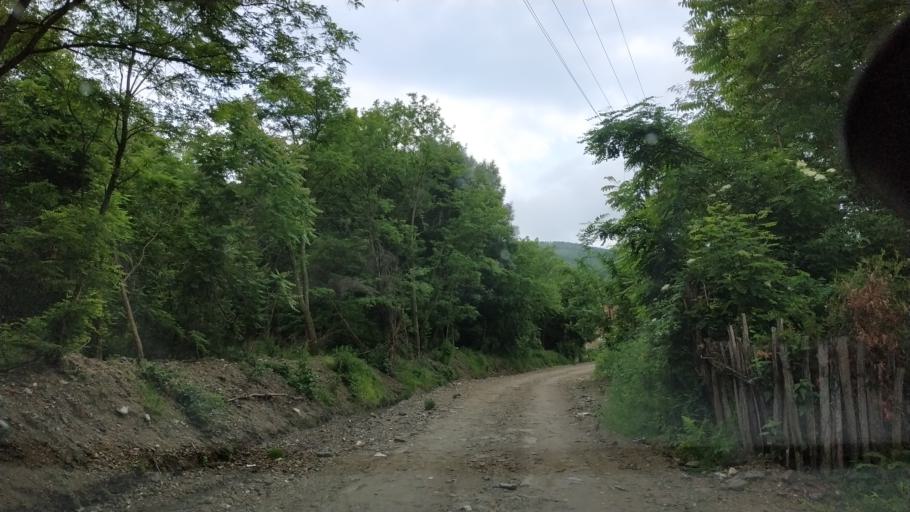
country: RS
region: Central Serbia
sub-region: Nisavski Okrug
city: Aleksinac
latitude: 43.4294
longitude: 21.6517
